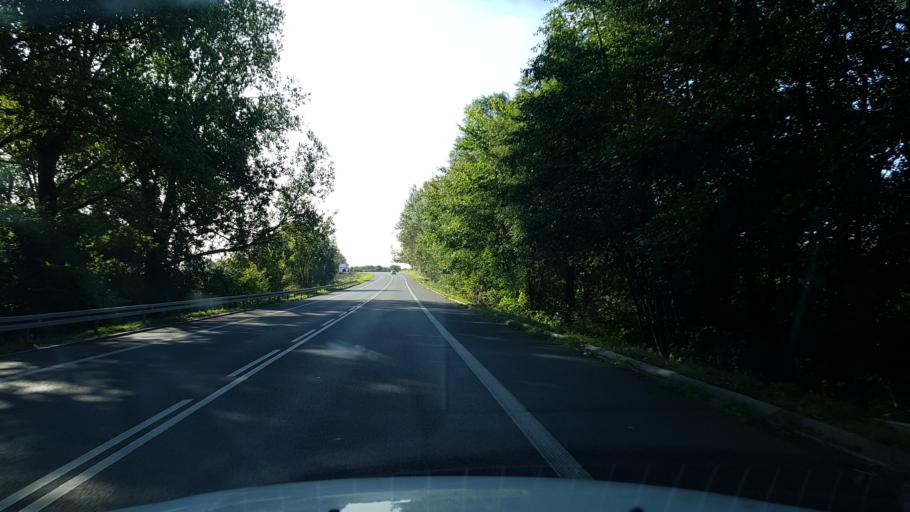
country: PL
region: West Pomeranian Voivodeship
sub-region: Powiat gryfinski
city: Stare Czarnowo
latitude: 53.2201
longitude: 14.7972
